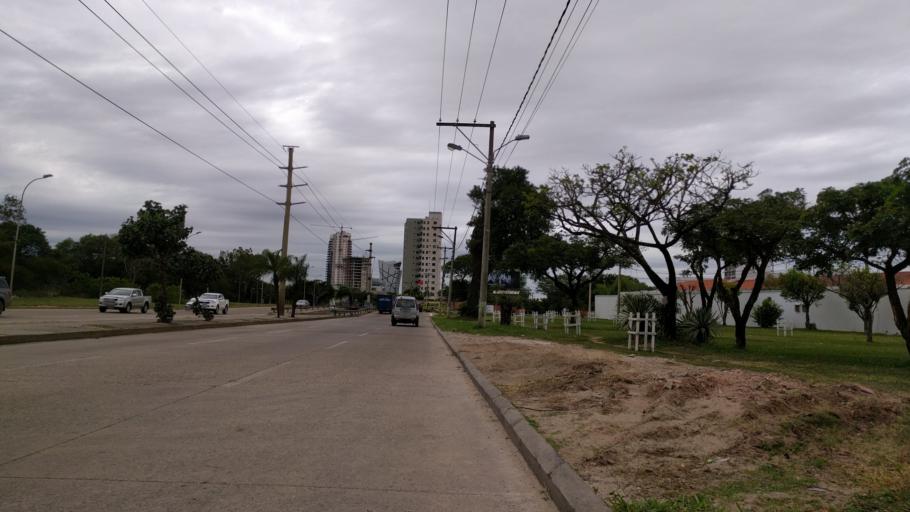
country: BO
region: Santa Cruz
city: Santa Cruz de la Sierra
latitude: -17.7667
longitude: -63.2062
